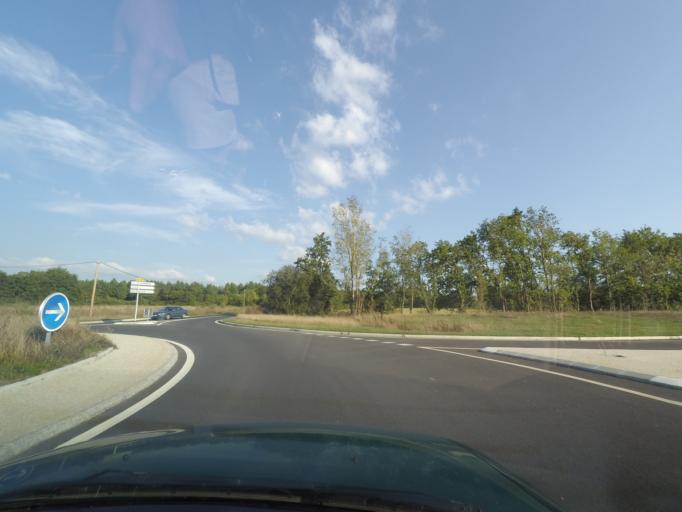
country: FR
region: Pays de la Loire
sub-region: Departement de la Loire-Atlantique
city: Saint-Philbert-de-Grand-Lieu
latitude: 47.0300
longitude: -1.6249
